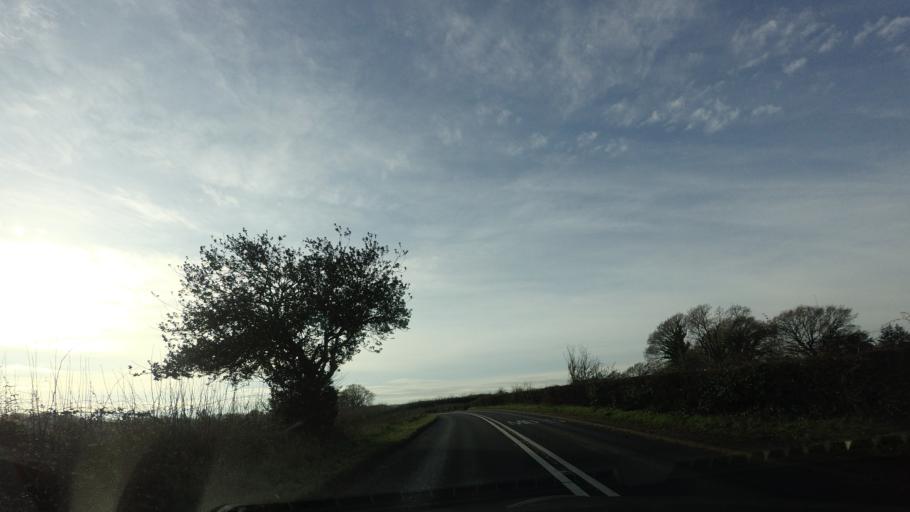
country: GB
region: England
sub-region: East Sussex
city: Battle
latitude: 50.8943
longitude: 0.4457
